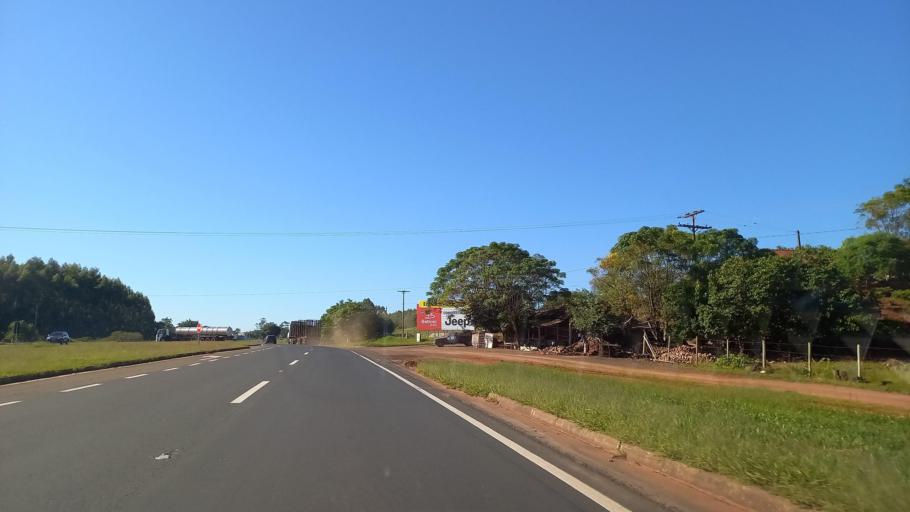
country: BR
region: Rio Grande do Sul
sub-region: Montenegro
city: Montenegro
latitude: -29.7793
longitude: -51.5564
